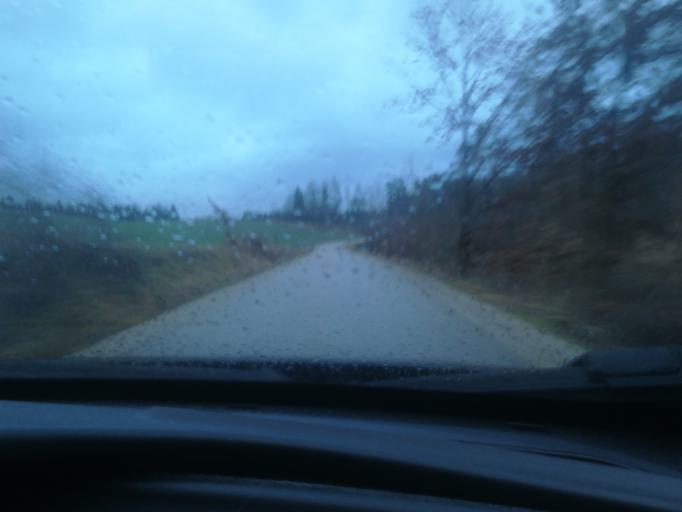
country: AT
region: Upper Austria
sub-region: Politischer Bezirk Perg
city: Perg
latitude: 48.3055
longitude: 14.6289
